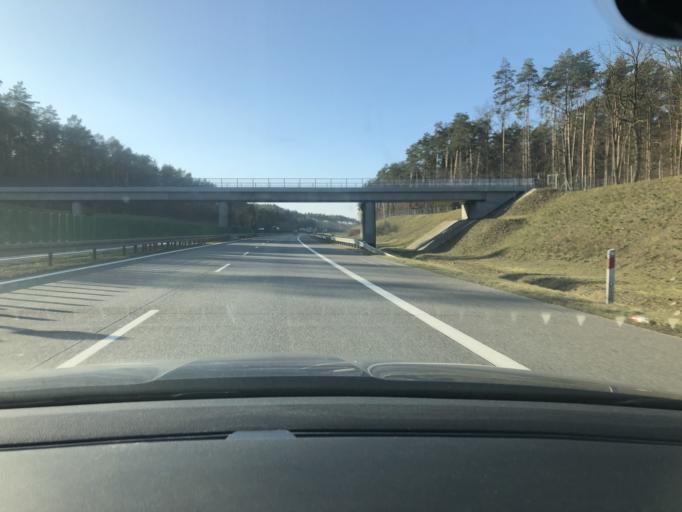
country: PL
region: Lubusz
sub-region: Powiat swiebodzinski
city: Lagow
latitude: 52.2947
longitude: 15.2869
